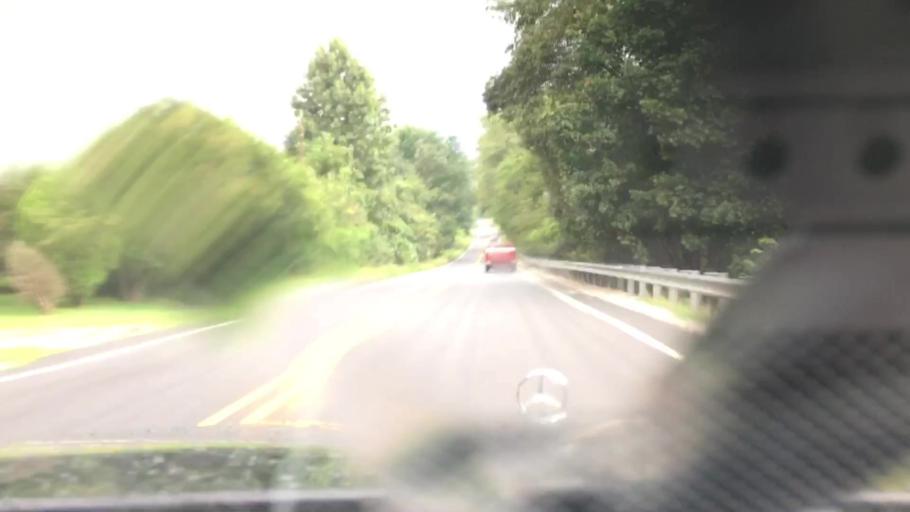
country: US
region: Virginia
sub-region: Nelson County
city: Nellysford
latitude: 37.9060
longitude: -78.8529
